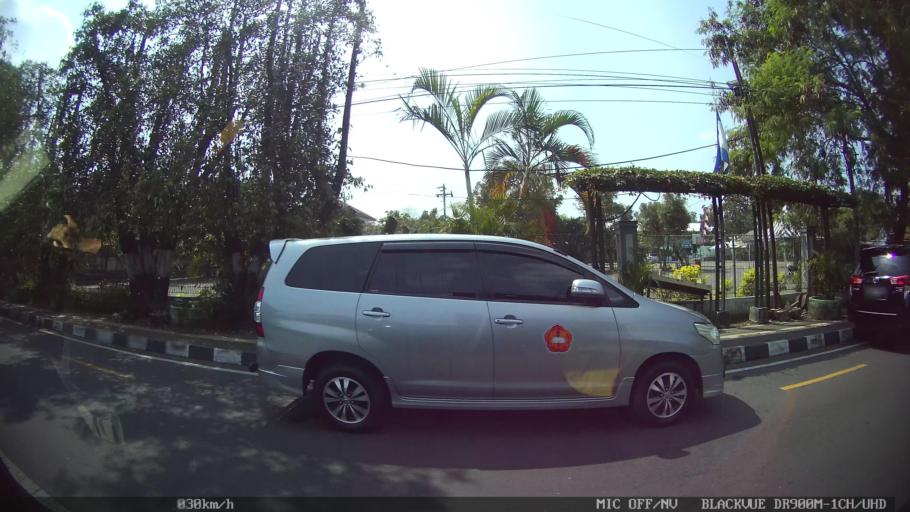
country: ID
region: Daerah Istimewa Yogyakarta
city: Yogyakarta
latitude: -7.8056
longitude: 110.3947
